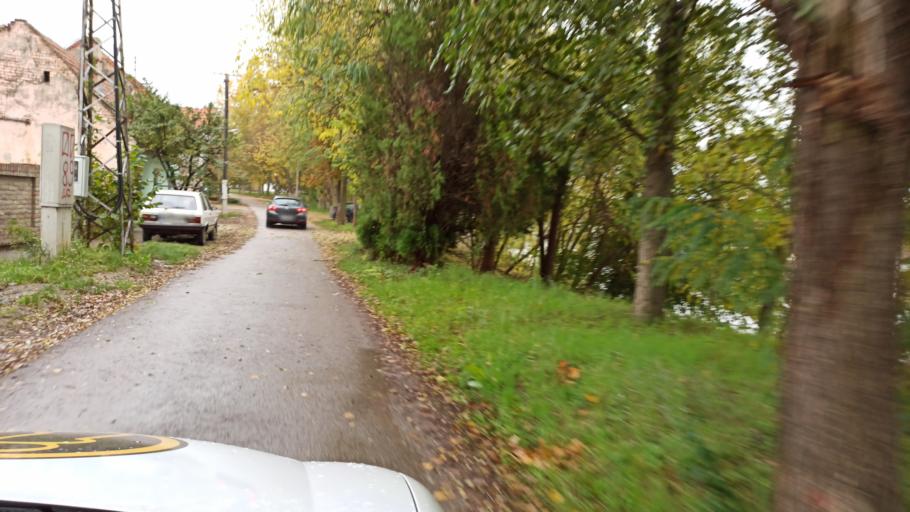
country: RS
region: Autonomna Pokrajina Vojvodina
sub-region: Srednjebanatski Okrug
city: Zrenjanin
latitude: 45.3745
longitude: 20.3927
